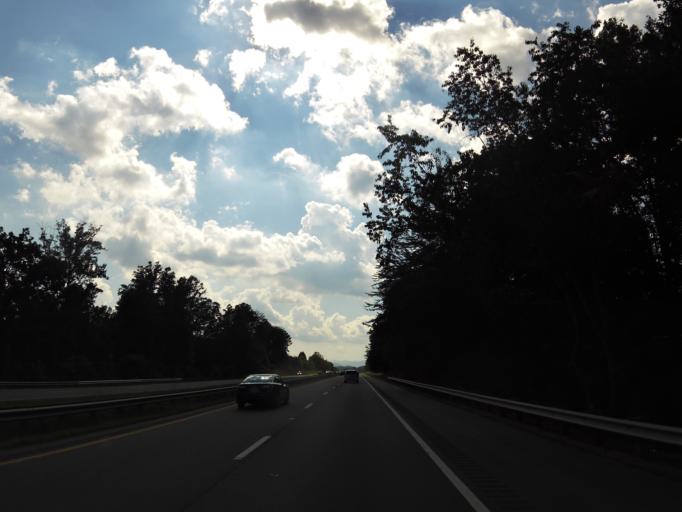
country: US
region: North Carolina
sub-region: McDowell County
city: West Marion
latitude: 35.6356
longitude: -82.0713
